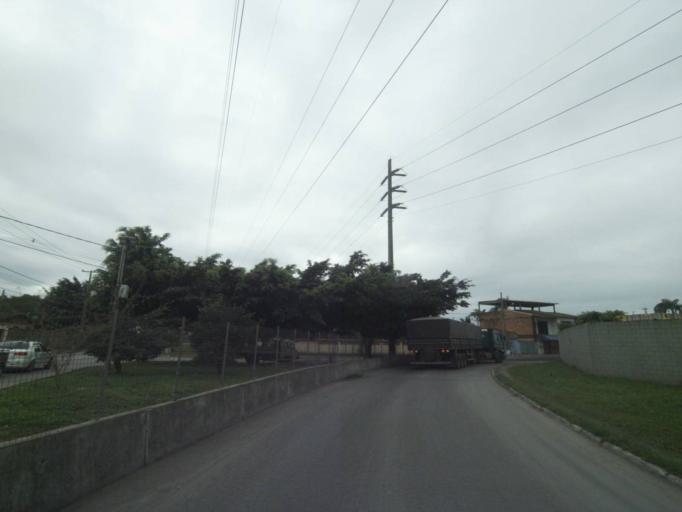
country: BR
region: Parana
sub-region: Paranagua
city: Paranagua
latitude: -25.5359
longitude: -48.5374
